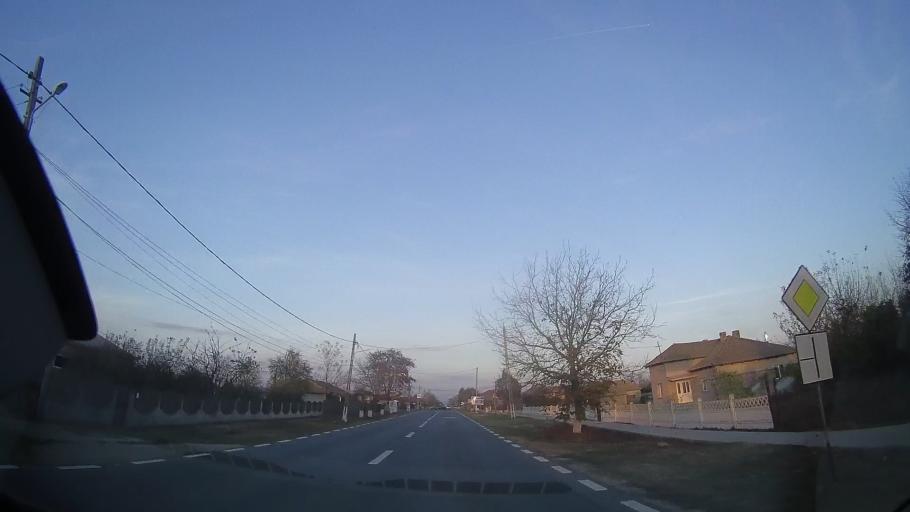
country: RO
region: Constanta
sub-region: Comuna Topraisar
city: Topraisar
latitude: 44.0099
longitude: 28.4469
